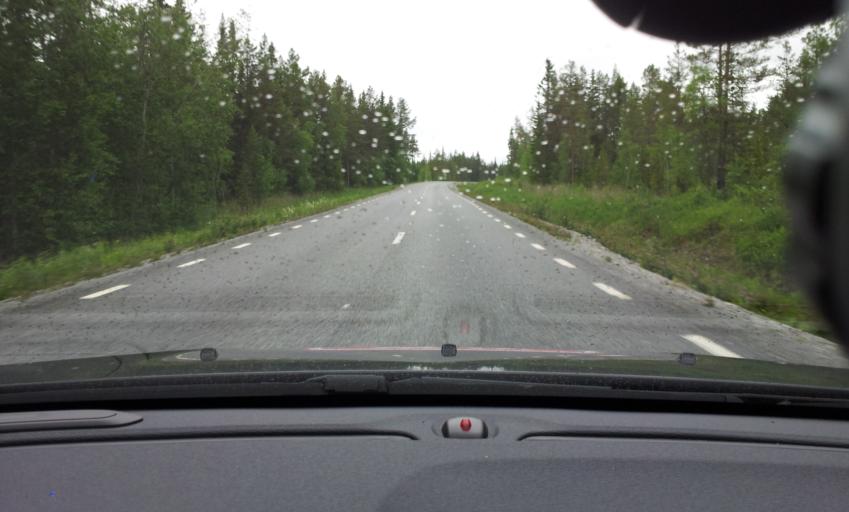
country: SE
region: Jaemtland
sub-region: OEstersunds Kommun
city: Lit
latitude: 63.6982
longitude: 14.6858
